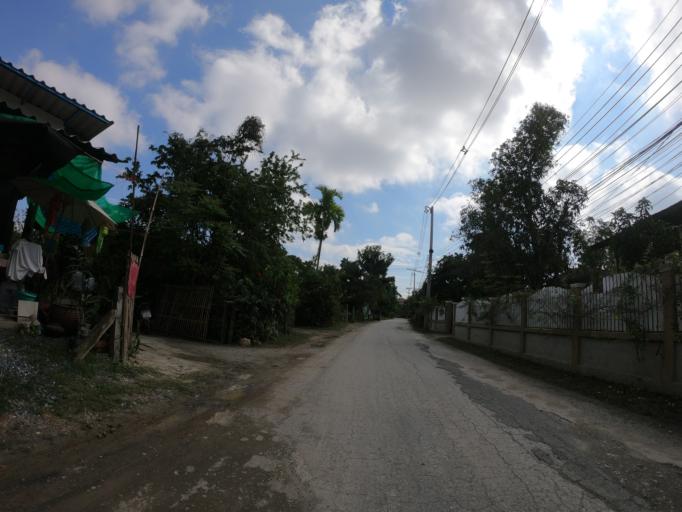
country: TH
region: Chiang Mai
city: San Sai
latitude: 18.8208
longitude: 99.0577
